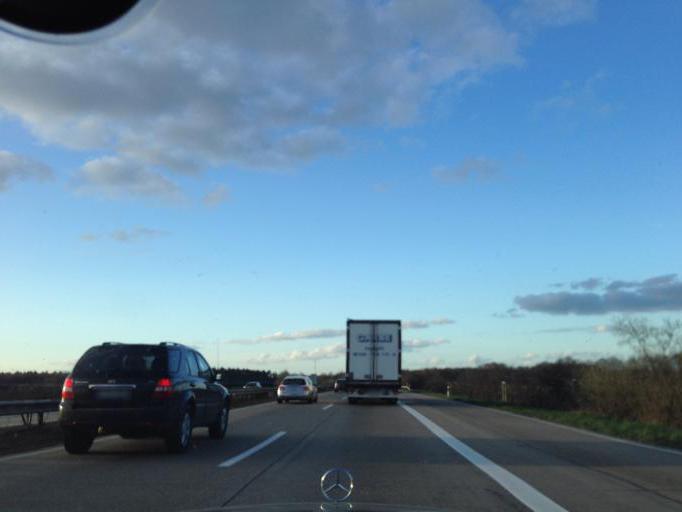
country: DE
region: Lower Saxony
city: Bad Fallingbostel
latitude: 52.8311
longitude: 9.6855
